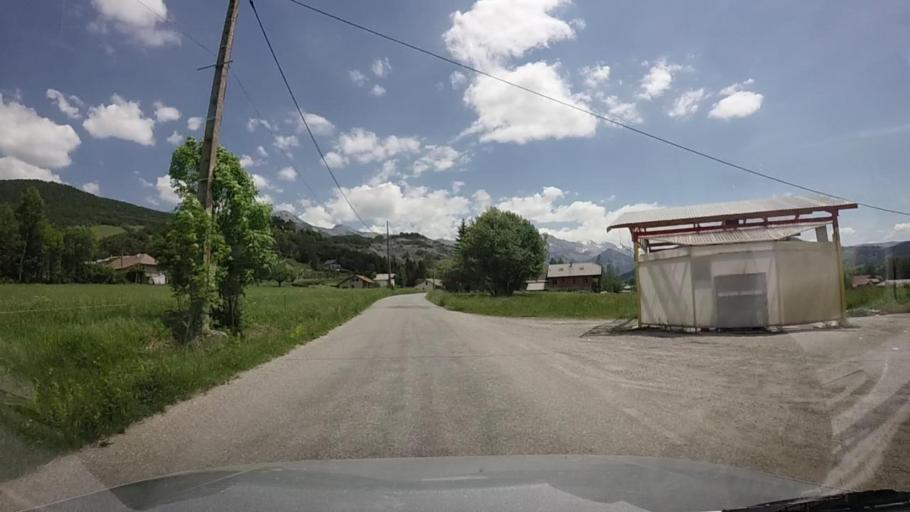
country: FR
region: Provence-Alpes-Cote d'Azur
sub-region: Departement des Alpes-de-Haute-Provence
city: Seyne-les-Alpes
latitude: 44.3553
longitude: 6.3394
